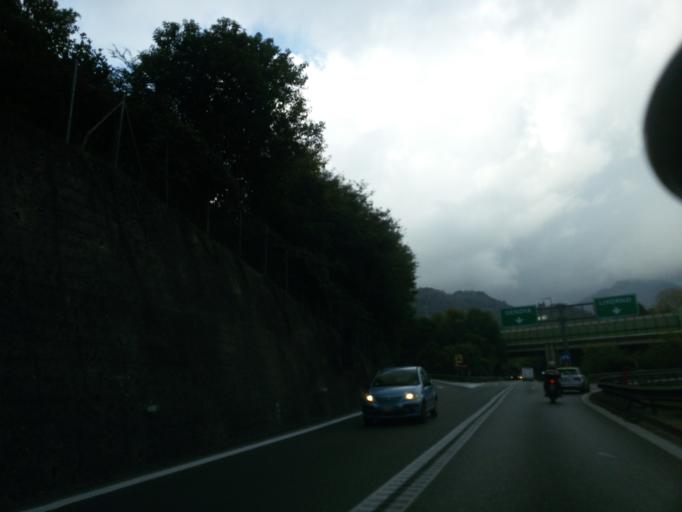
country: IT
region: Liguria
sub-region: Provincia di Genova
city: Rapallo
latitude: 44.3575
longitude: 9.2094
